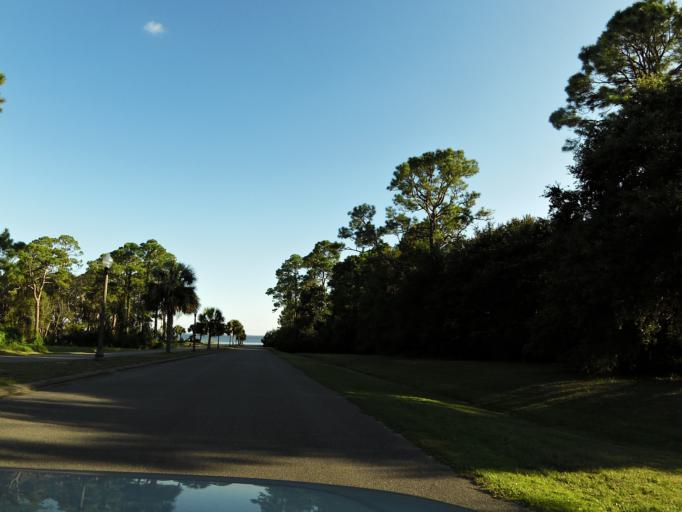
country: US
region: Florida
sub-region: Franklin County
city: Eastpoint
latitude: 29.7601
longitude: -84.8305
